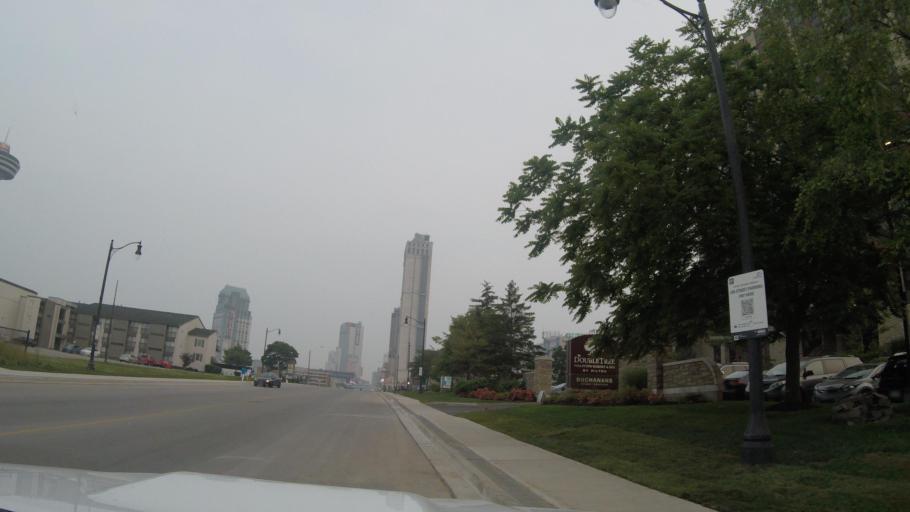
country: CA
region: Ontario
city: Niagara Falls
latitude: 43.0877
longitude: -79.0833
